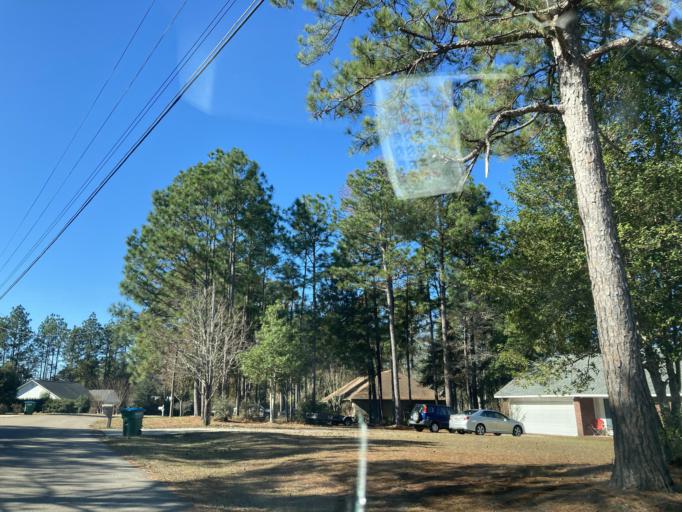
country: US
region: Mississippi
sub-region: Forrest County
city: Petal
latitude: 31.3536
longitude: -89.1992
